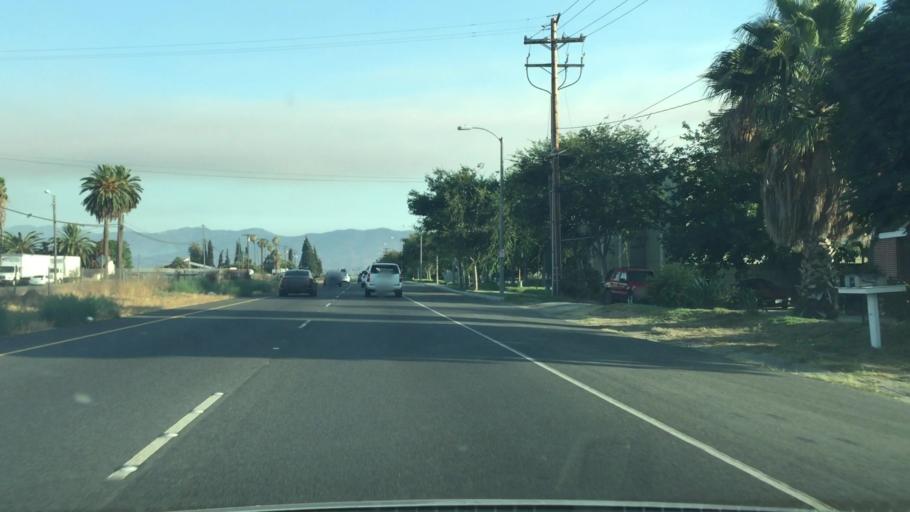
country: US
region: California
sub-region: San Bernardino County
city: Chino
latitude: 33.9961
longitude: -117.6509
